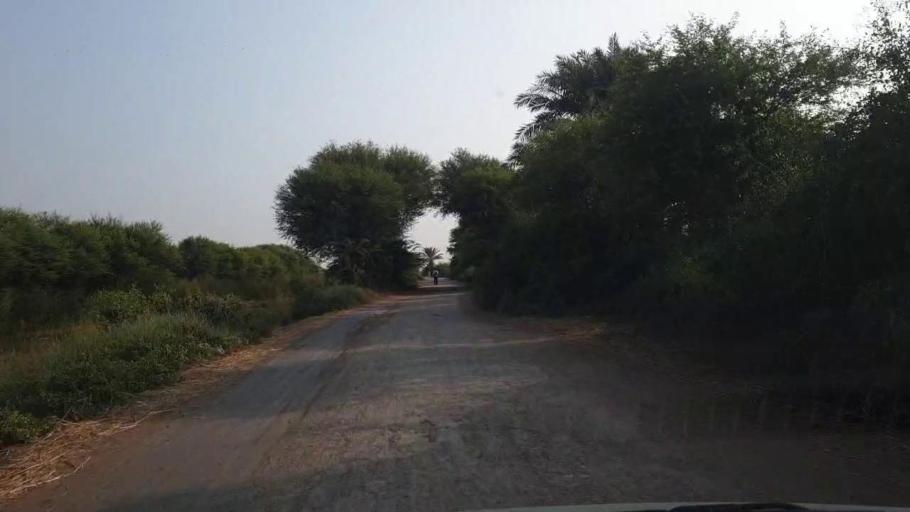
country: PK
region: Sindh
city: Matli
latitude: 25.0636
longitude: 68.7603
